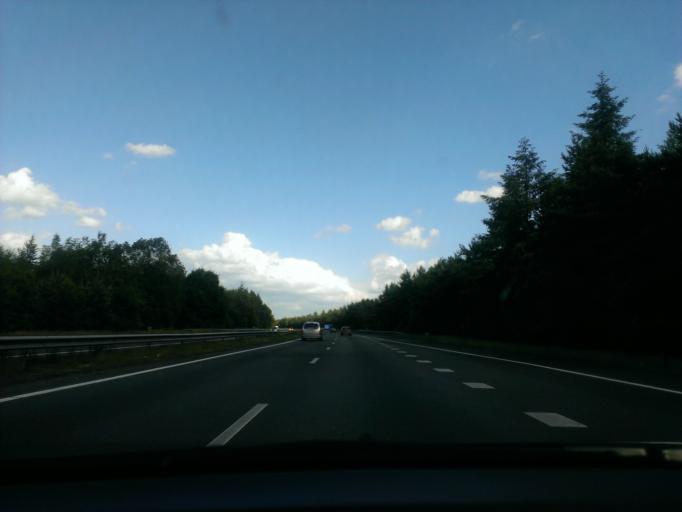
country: NL
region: Gelderland
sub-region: Gemeente Apeldoorn
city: Beekbergen
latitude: 52.1753
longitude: 5.9485
